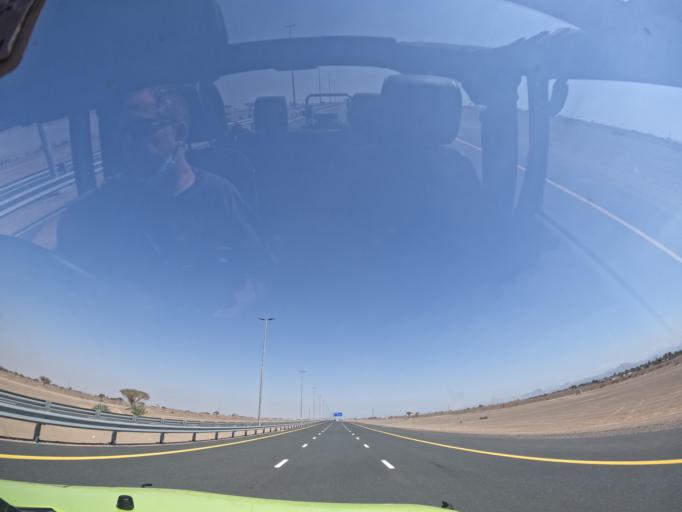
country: AE
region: Ash Shariqah
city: Adh Dhayd
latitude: 25.0931
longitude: 55.9229
